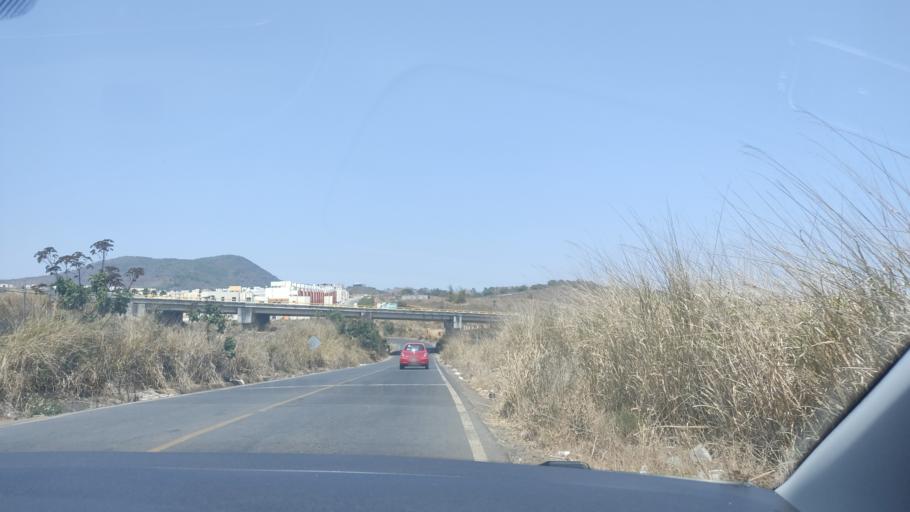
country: MX
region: Nayarit
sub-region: Tepic
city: La Corregidora
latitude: 21.4926
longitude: -104.8128
